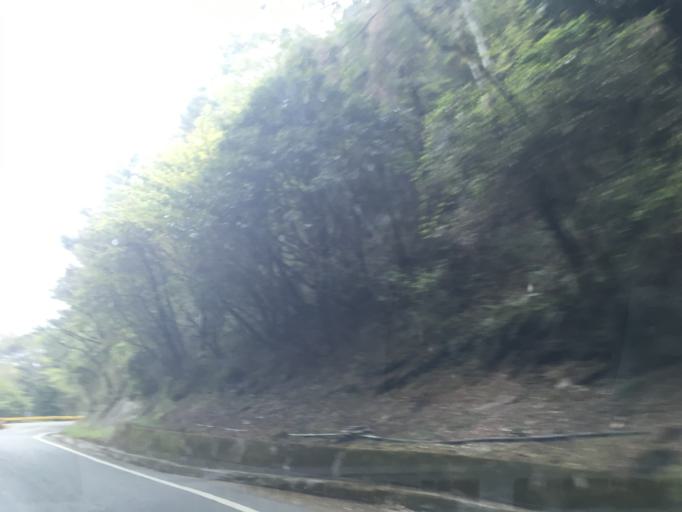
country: TW
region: Taiwan
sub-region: Hualien
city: Hualian
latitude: 24.1825
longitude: 121.3237
